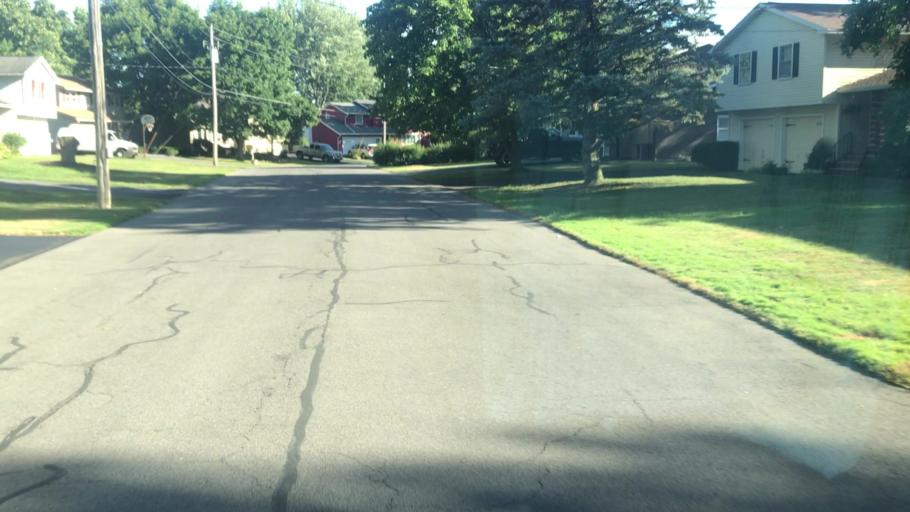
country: US
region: New York
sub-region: Onondaga County
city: Liverpool
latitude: 43.1342
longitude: -76.2162
